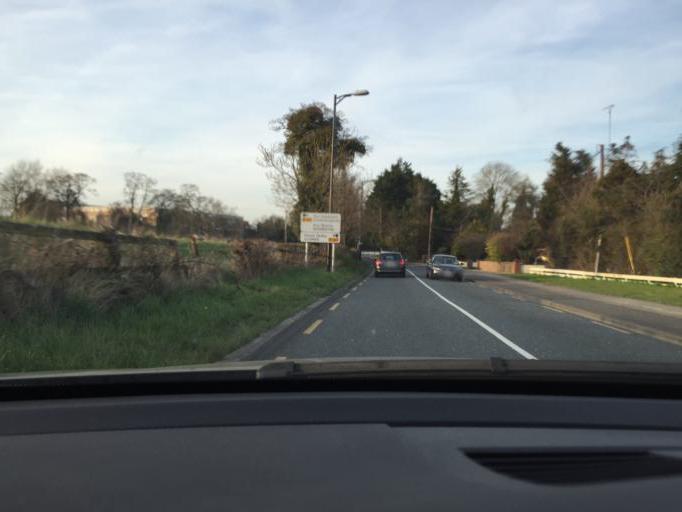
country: IE
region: Leinster
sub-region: An Mhi
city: Dunboyne
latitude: 53.4094
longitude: -6.4450
